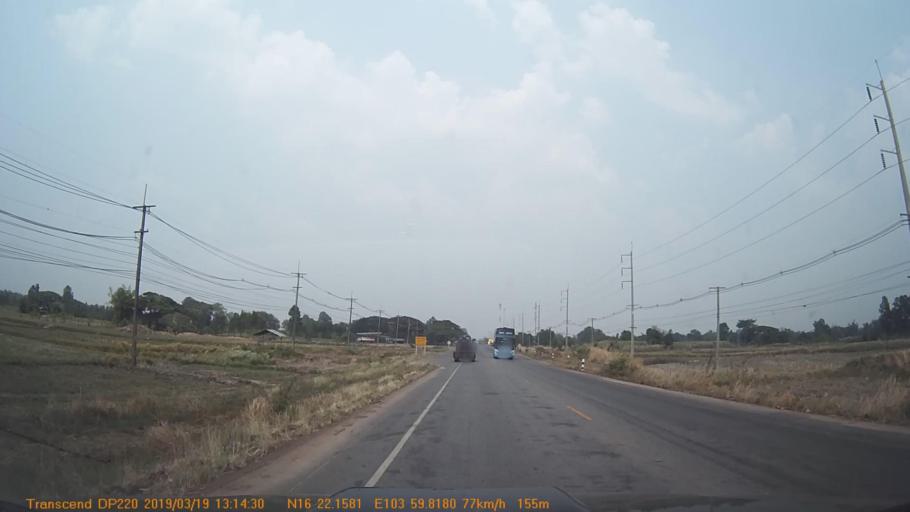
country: TH
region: Roi Et
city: Waeng
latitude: 16.3695
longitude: 103.9970
